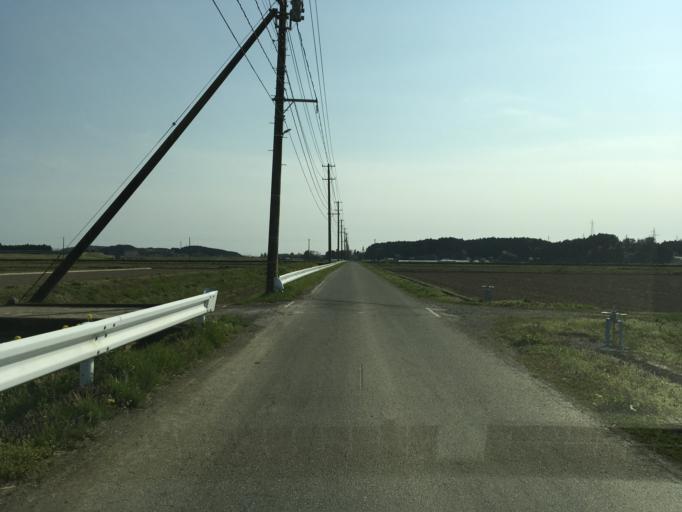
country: JP
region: Miyagi
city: Wakuya
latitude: 38.7307
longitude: 141.2914
